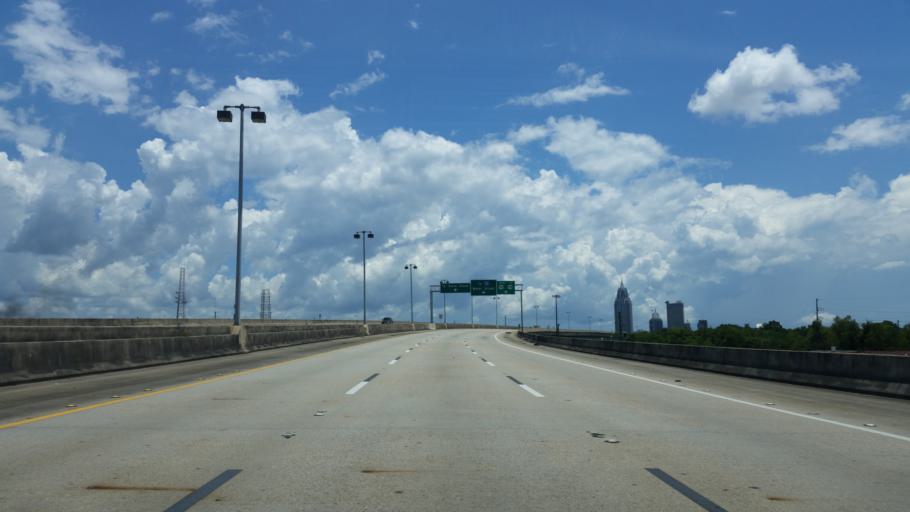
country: US
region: Alabama
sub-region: Mobile County
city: Mobile
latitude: 30.7115
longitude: -88.0533
